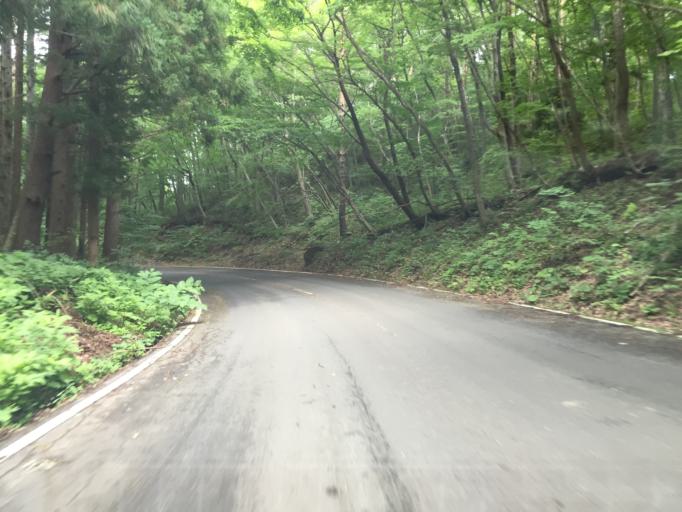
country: JP
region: Fukushima
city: Nihommatsu
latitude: 37.6761
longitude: 140.3356
